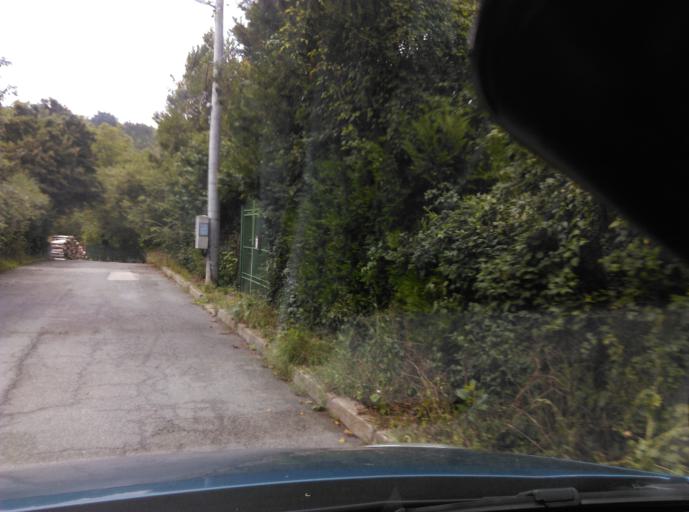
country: BG
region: Sofia-Capital
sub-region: Stolichna Obshtina
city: Sofia
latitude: 42.5987
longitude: 23.4034
